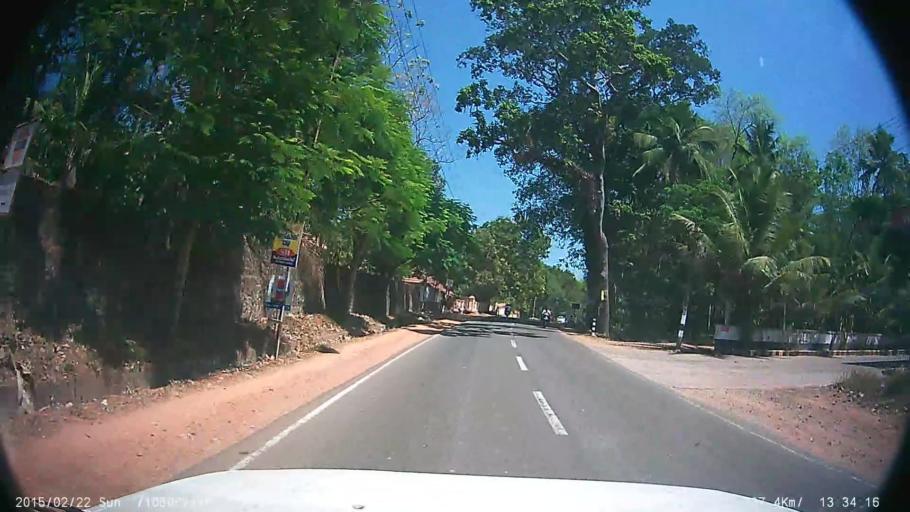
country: IN
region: Kerala
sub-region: Kottayam
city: Changanacheri
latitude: 9.4806
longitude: 76.5986
